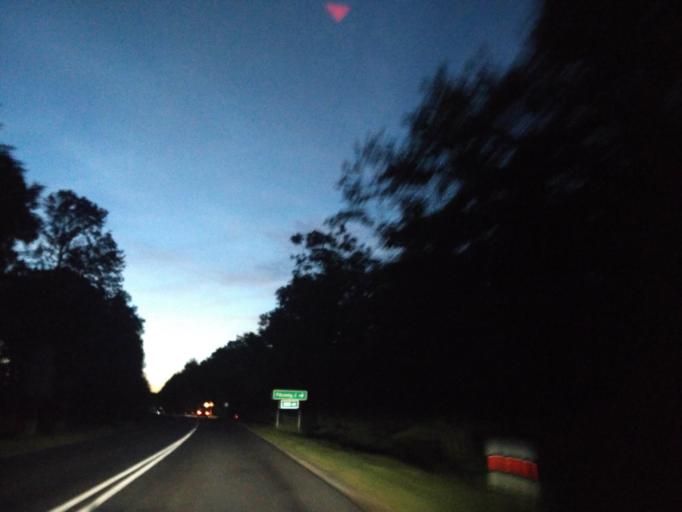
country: HU
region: Vas
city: Vasvar
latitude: 47.0070
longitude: 16.8286
